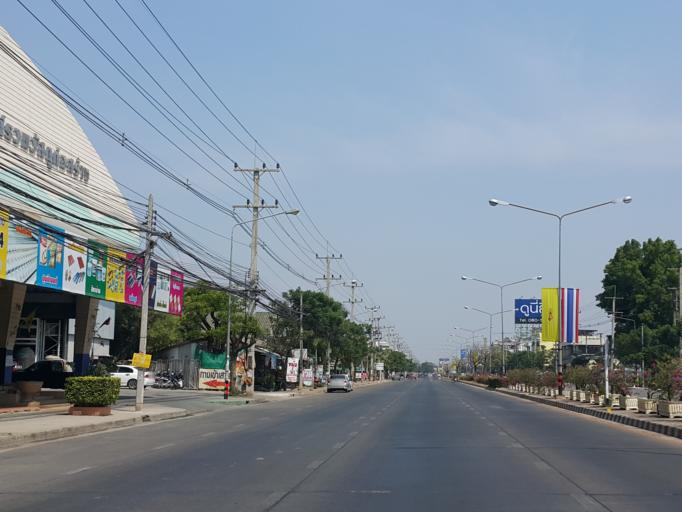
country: TH
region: Phitsanulok
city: Phitsanulok
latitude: 16.8300
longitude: 100.2505
